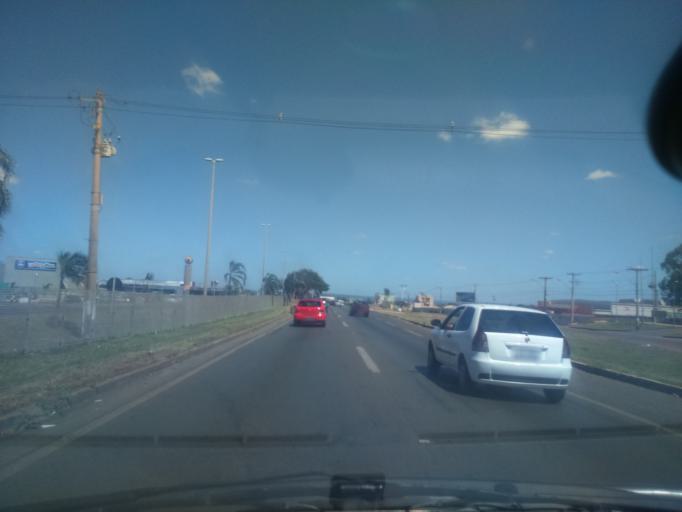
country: BR
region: Goias
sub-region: Luziania
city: Luziania
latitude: -16.0782
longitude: -47.9861
